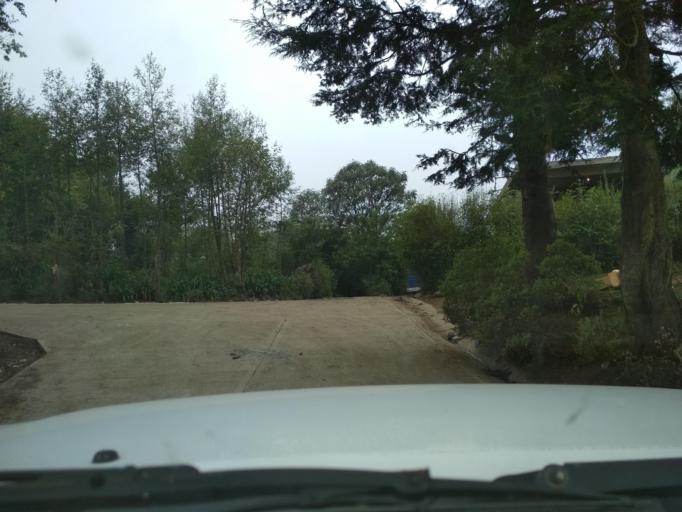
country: MX
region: Veracruz
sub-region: La Perla
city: Chilapa
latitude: 18.9728
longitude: -97.1971
